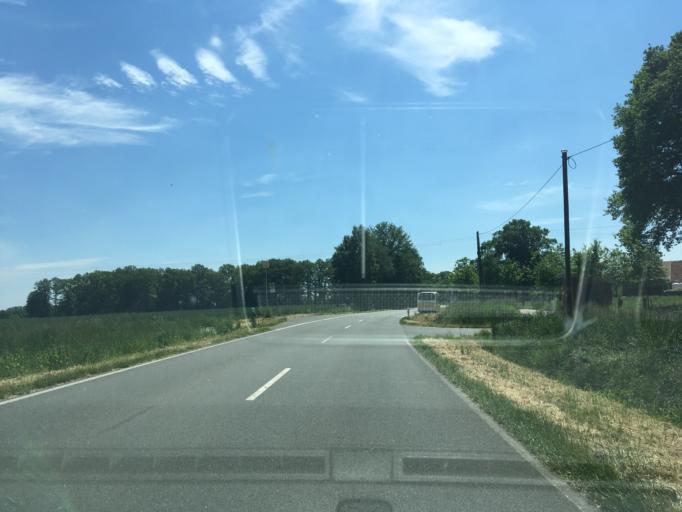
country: DE
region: North Rhine-Westphalia
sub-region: Regierungsbezirk Munster
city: Borken
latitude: 51.8813
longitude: 6.8277
